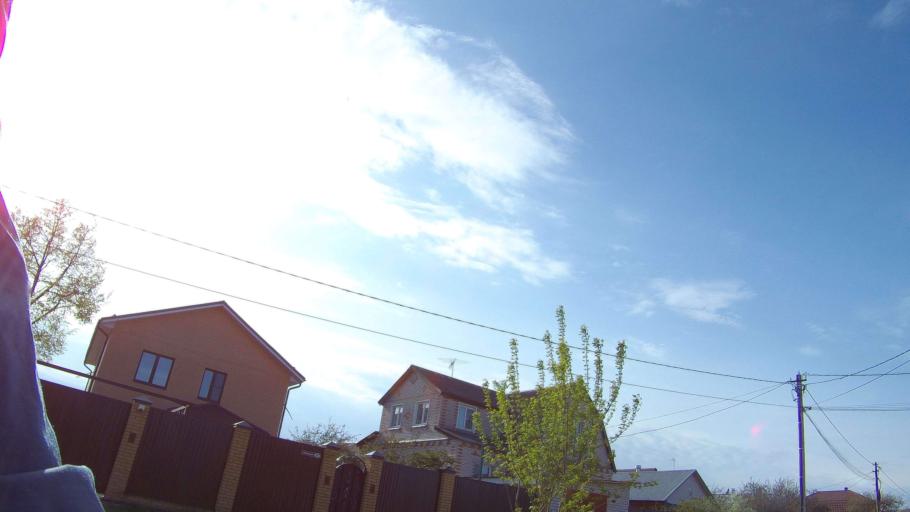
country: RU
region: Moskovskaya
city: Ramenskoye
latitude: 55.5493
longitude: 38.2366
